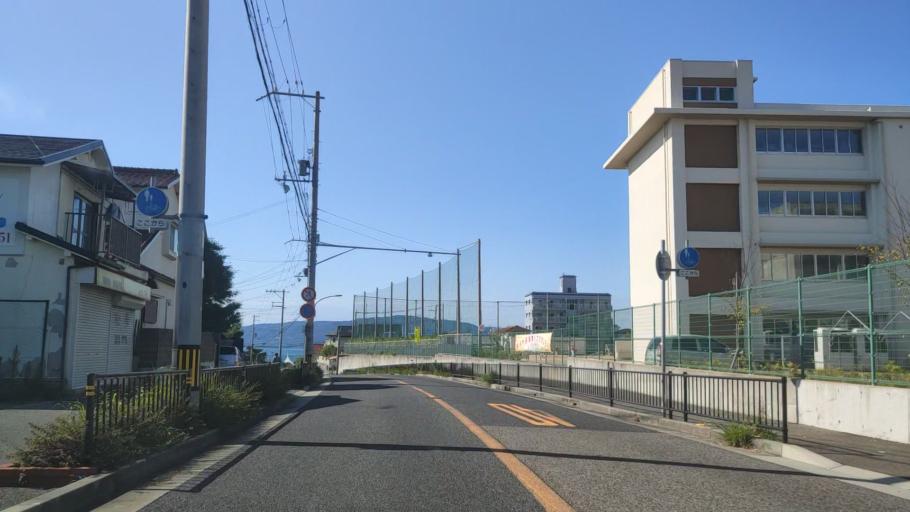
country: JP
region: Hyogo
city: Akashi
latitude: 34.6507
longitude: 135.0060
